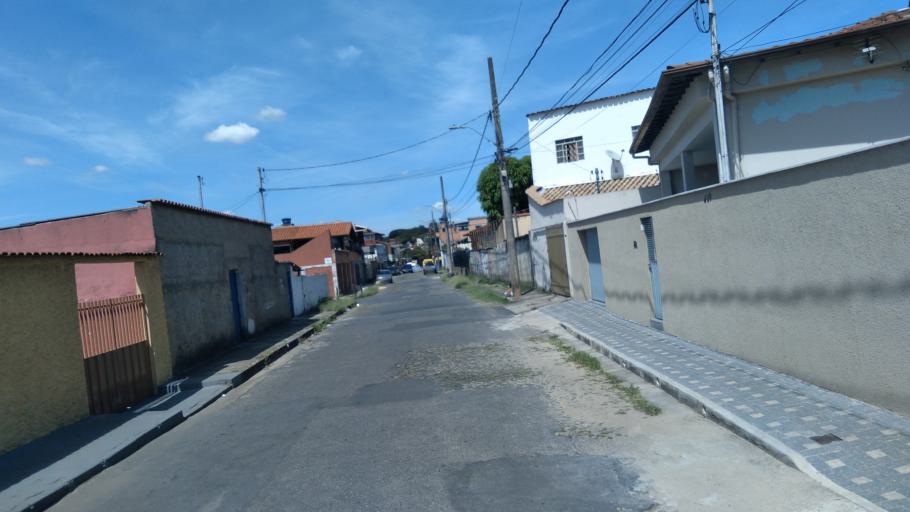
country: BR
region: Minas Gerais
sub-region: Contagem
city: Contagem
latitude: -19.8936
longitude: -44.0183
